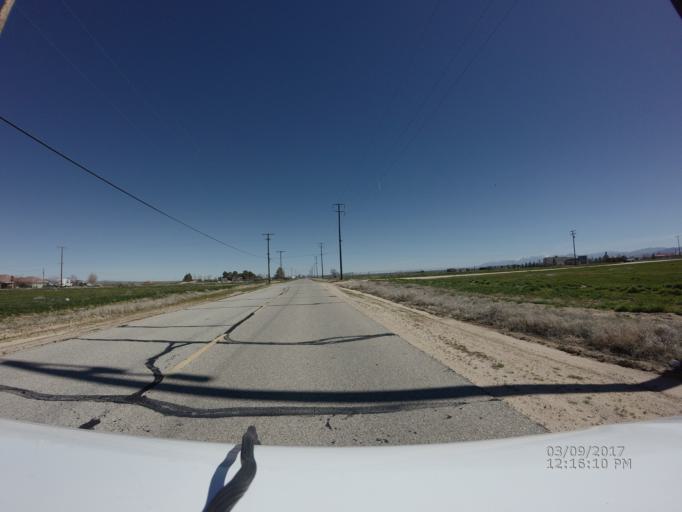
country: US
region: California
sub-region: Los Angeles County
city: Quartz Hill
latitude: 34.7330
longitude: -118.2644
